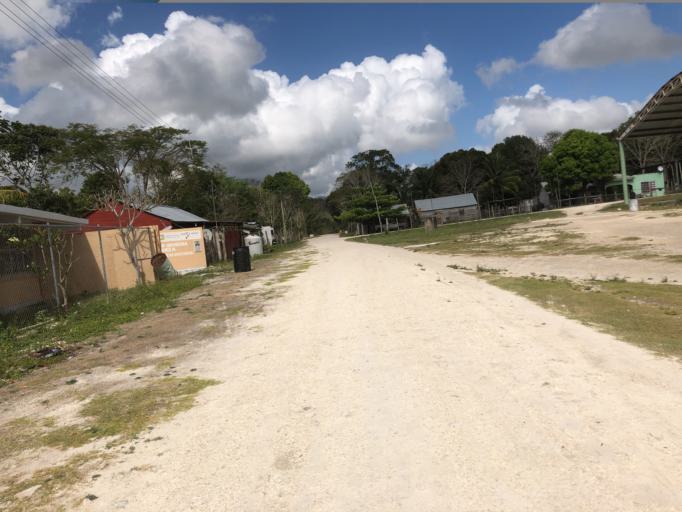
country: MX
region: Quintana Roo
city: Nicolas Bravo
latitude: 18.4512
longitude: -89.3076
